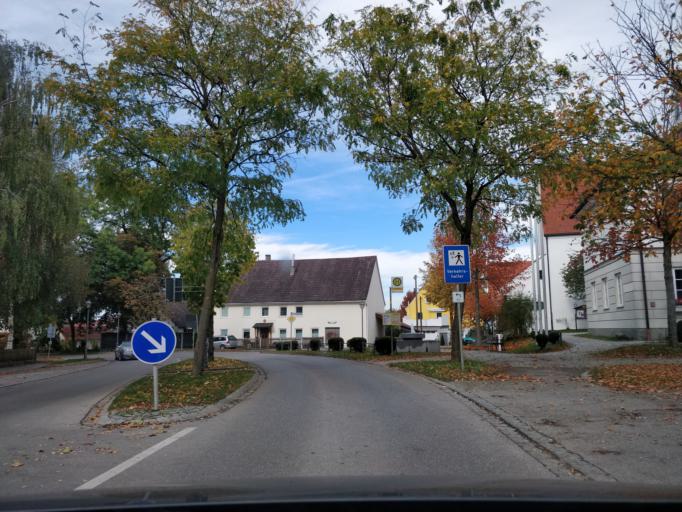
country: DE
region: Bavaria
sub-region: Swabia
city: Wiedergeltingen
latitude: 48.0393
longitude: 10.6711
